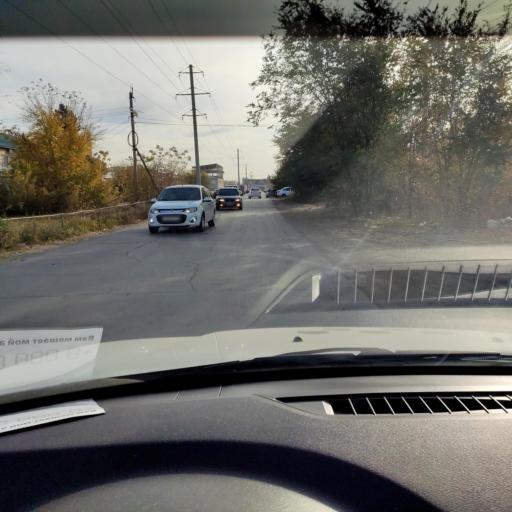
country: RU
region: Samara
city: Tol'yatti
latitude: 53.5466
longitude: 49.4337
